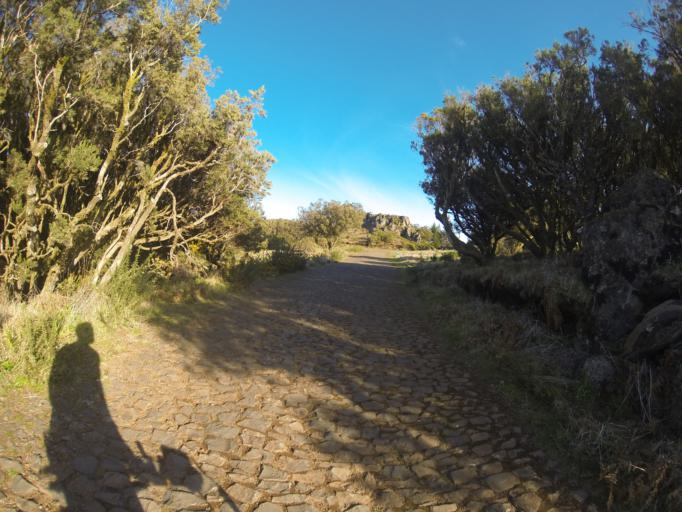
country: PT
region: Madeira
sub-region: Sao Vicente
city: Sao Vicente
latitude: 32.7573
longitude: -17.0584
